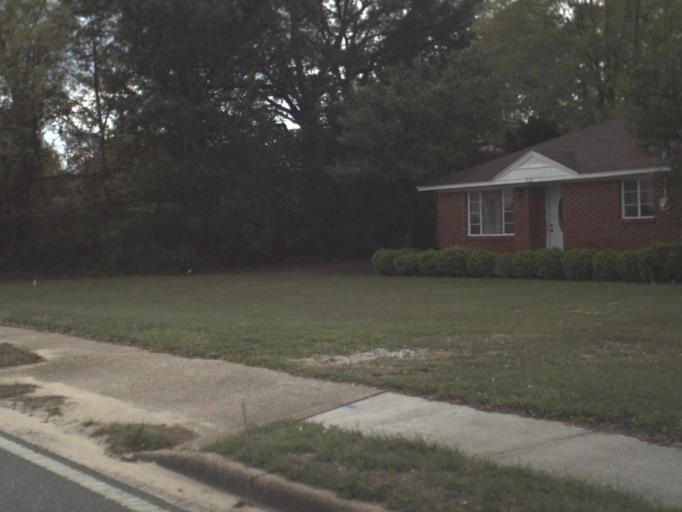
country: US
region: Florida
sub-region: Okaloosa County
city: Crestview
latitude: 30.7758
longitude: -86.5635
